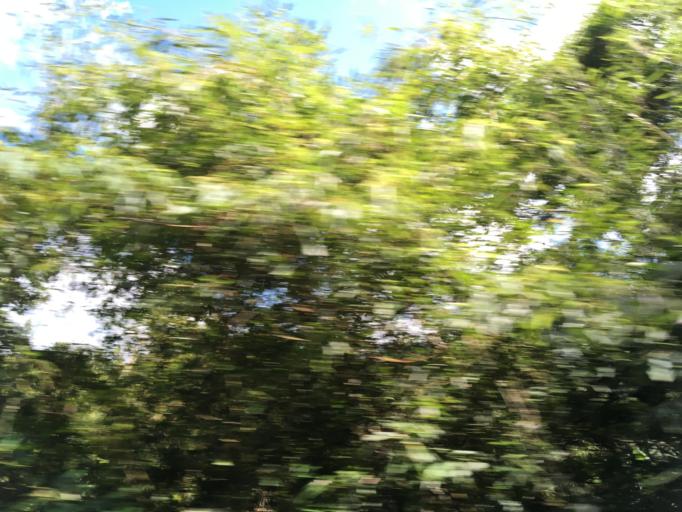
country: TW
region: Taipei
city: Taipei
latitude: 24.9391
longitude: 121.5784
